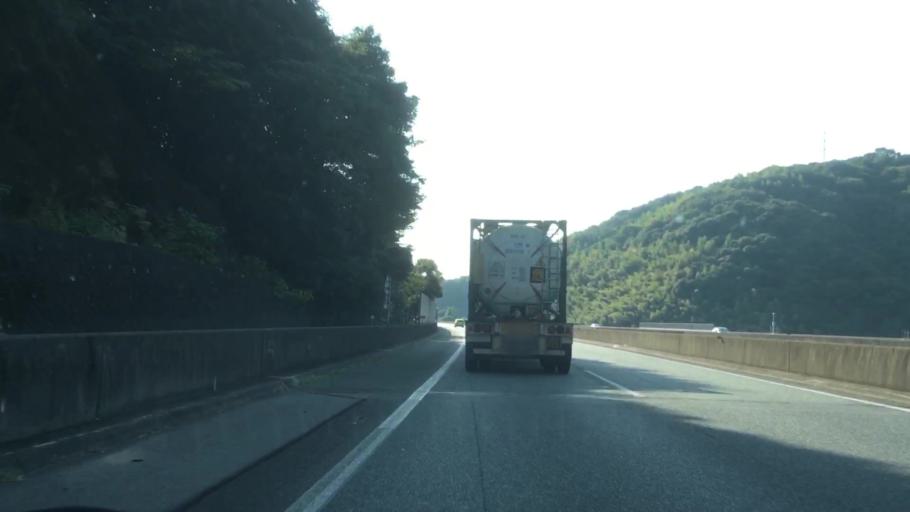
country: JP
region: Yamaguchi
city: Kudamatsu
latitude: 34.0441
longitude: 131.8682
